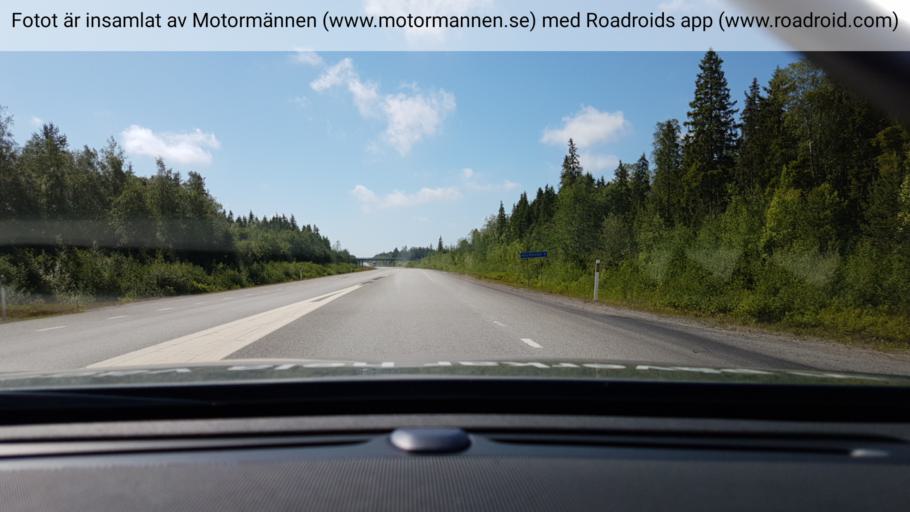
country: SE
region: Vaesterbotten
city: Obbola
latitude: 63.7651
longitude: 20.2955
